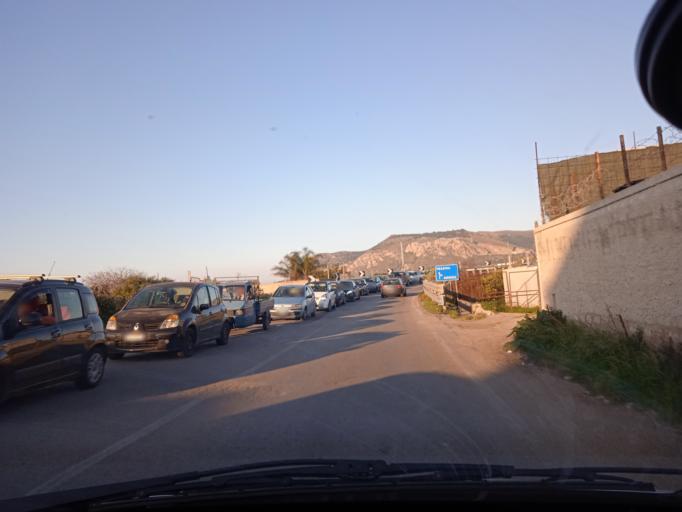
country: IT
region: Sicily
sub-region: Palermo
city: Ficarazzi
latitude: 38.0916
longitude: 13.4761
